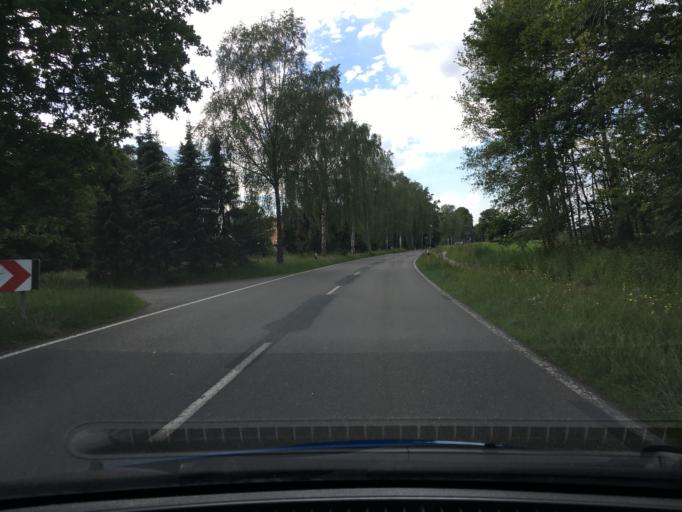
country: DE
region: Lower Saxony
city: Otter
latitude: 53.2576
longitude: 9.7436
